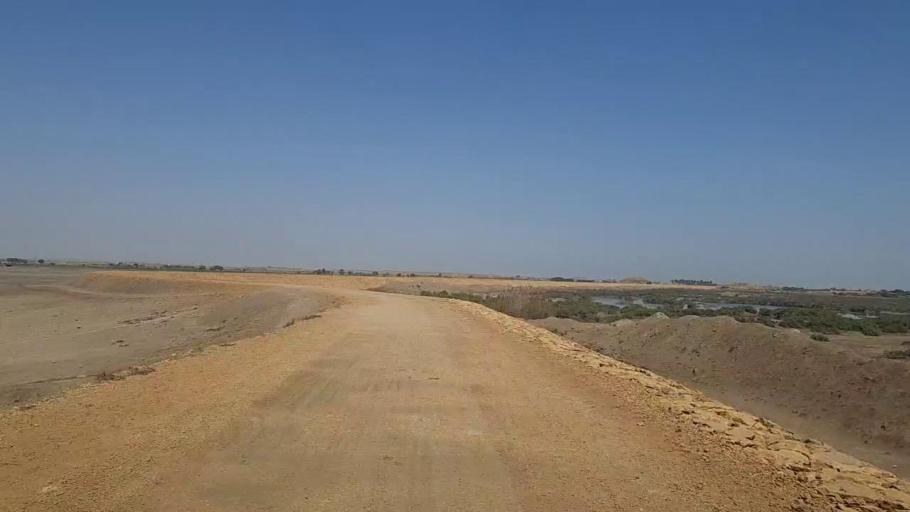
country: PK
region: Sindh
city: Thatta
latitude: 24.7985
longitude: 67.9988
